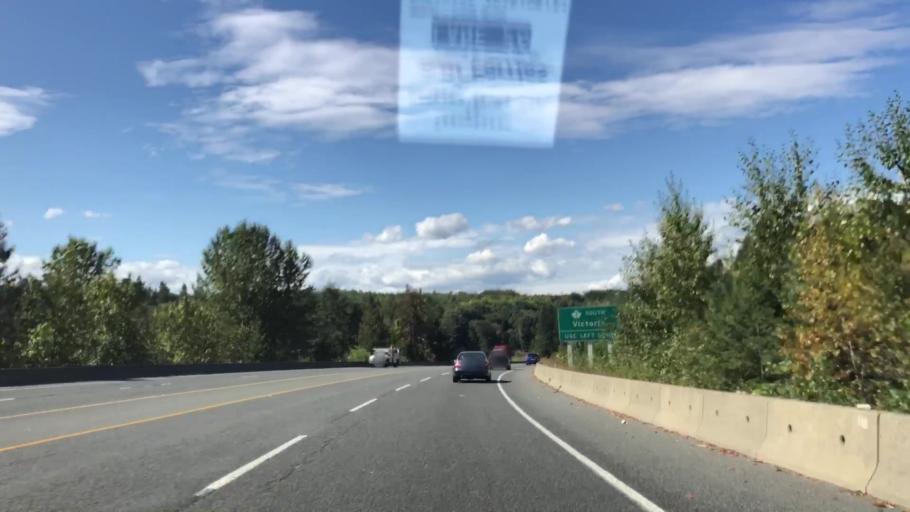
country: CA
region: British Columbia
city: Nanaimo
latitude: 49.1137
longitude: -123.8808
